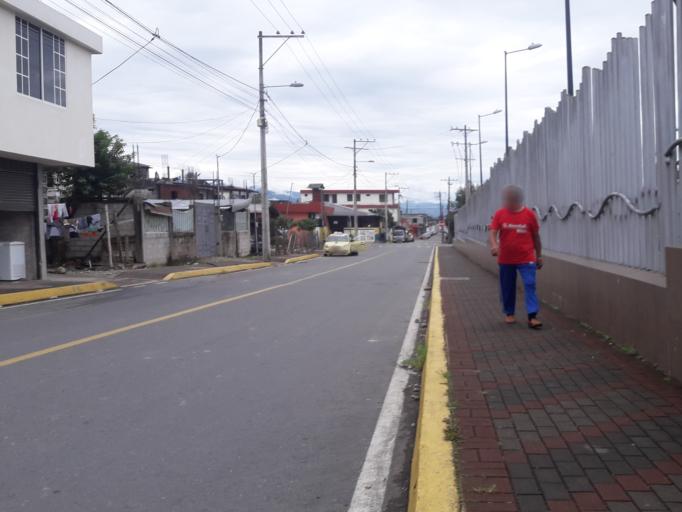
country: EC
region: Napo
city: Tena
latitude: -1.0049
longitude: -77.8123
